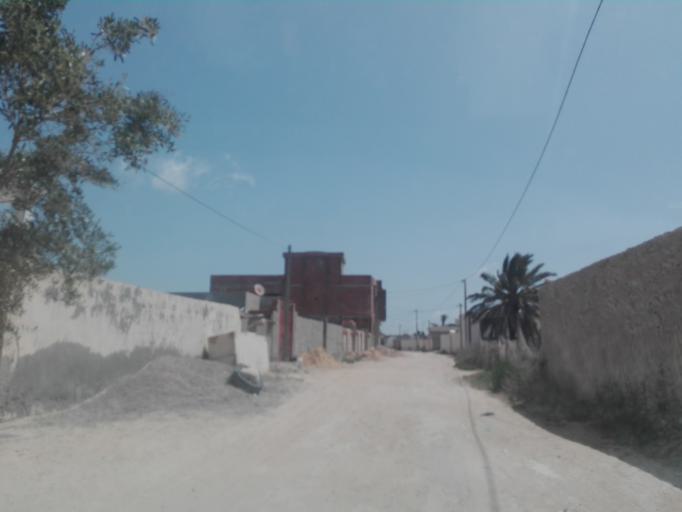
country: TN
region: Safaqis
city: Al Qarmadah
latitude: 34.6519
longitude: 11.0386
